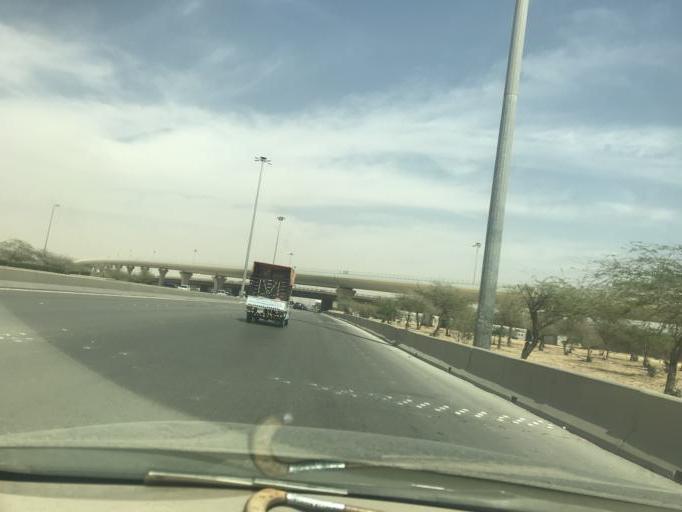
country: SA
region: Ar Riyad
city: Riyadh
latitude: 24.8244
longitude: 46.7163
